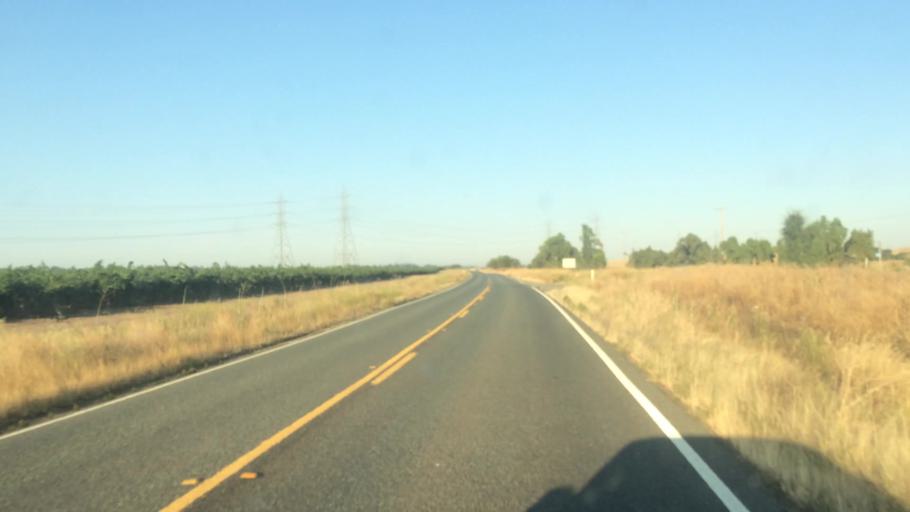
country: US
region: California
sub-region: Sacramento County
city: Clay
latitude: 38.3410
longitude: -121.1373
